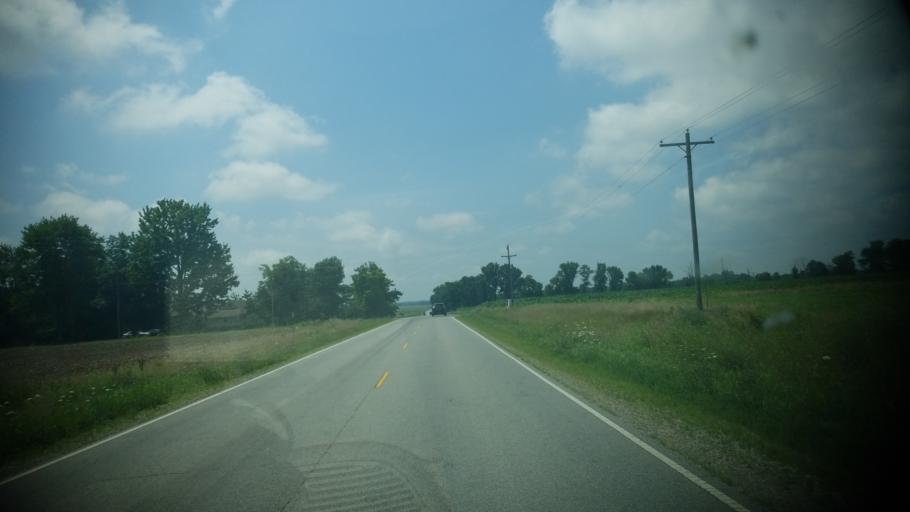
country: US
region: Illinois
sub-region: Wayne County
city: Fairfield
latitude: 38.4692
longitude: -88.3490
